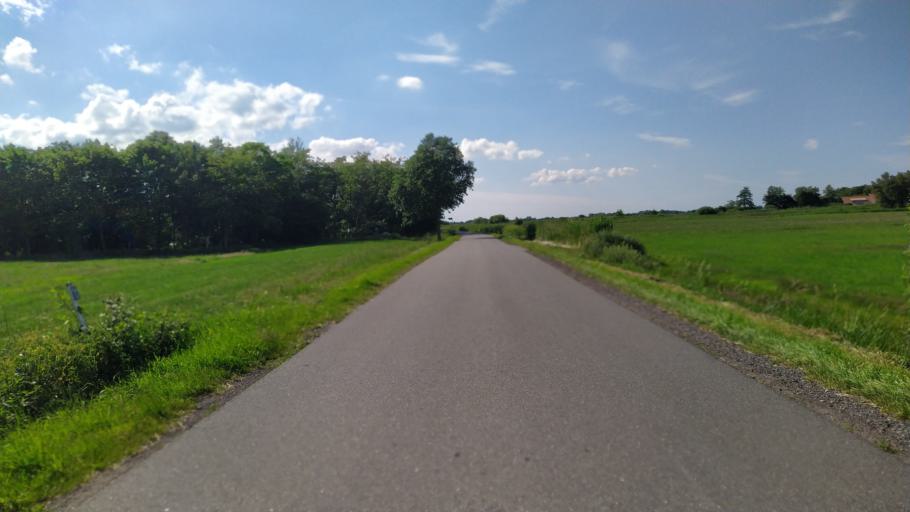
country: DE
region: Lower Saxony
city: Odisheim
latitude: 53.6696
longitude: 8.9213
